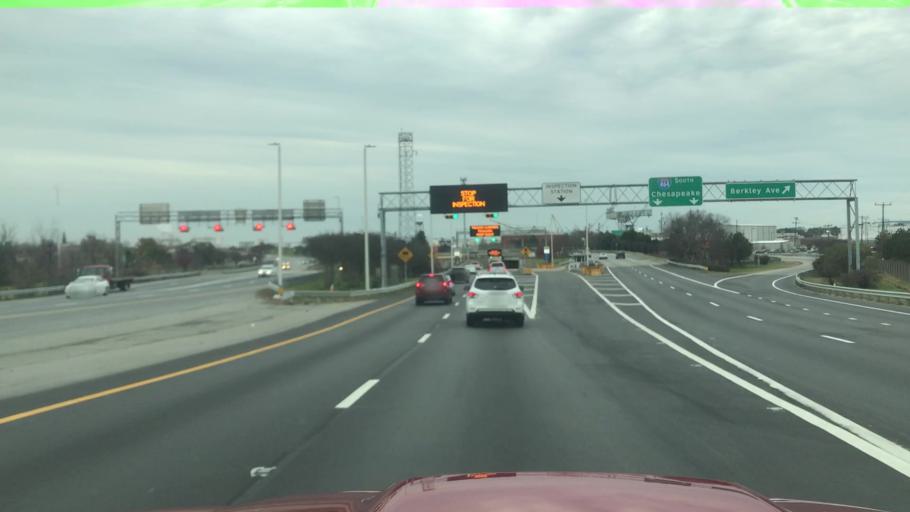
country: US
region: Virginia
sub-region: City of Norfolk
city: Norfolk
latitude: 36.8389
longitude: -76.2871
